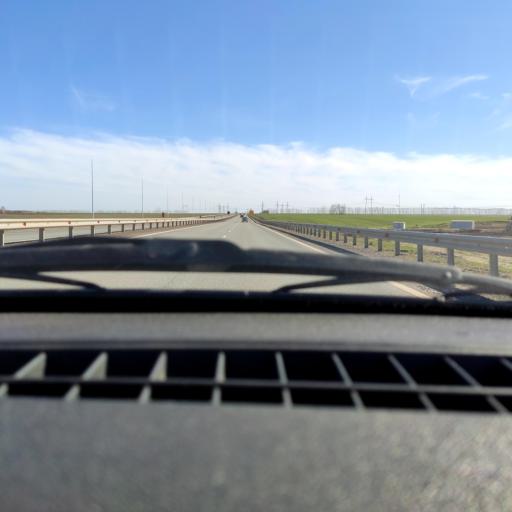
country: RU
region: Bashkortostan
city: Tolbazy
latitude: 54.2583
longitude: 55.8812
